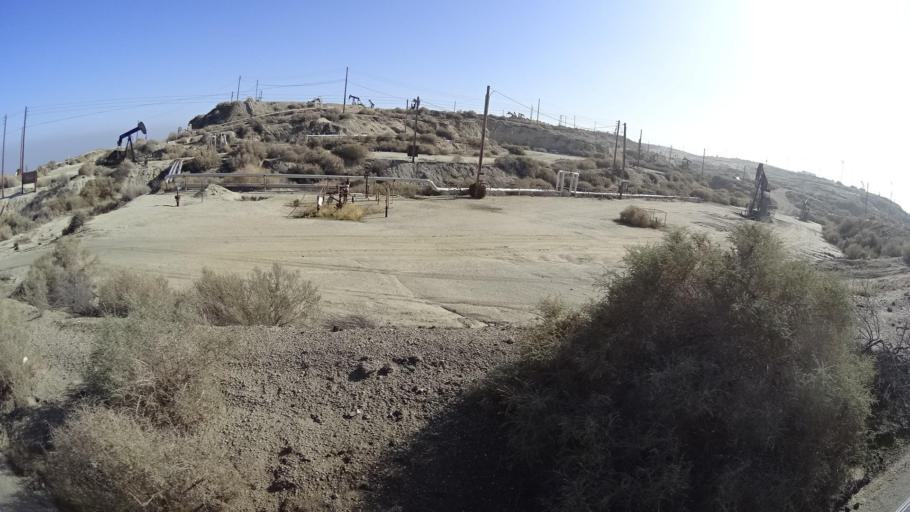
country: US
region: California
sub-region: Kern County
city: Taft Heights
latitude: 35.1205
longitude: -119.4770
